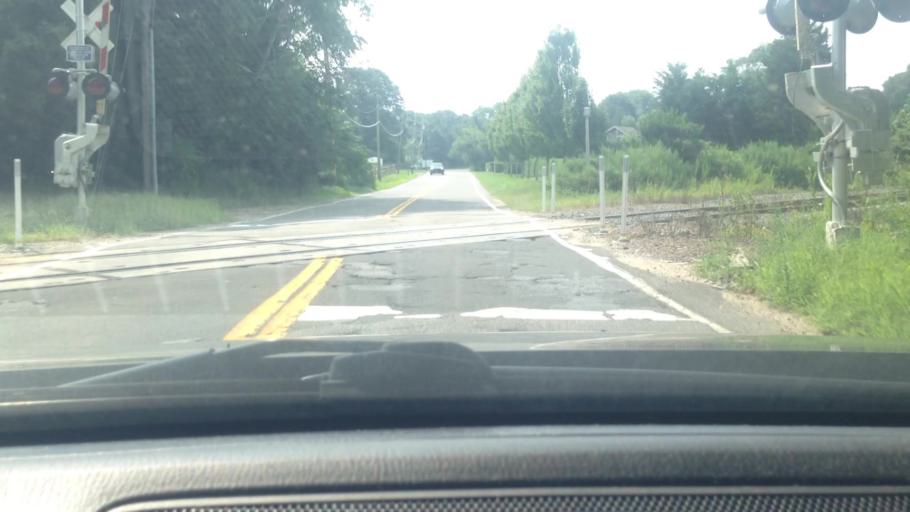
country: US
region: New York
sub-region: Suffolk County
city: Water Mill
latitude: 40.9223
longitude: -72.3428
